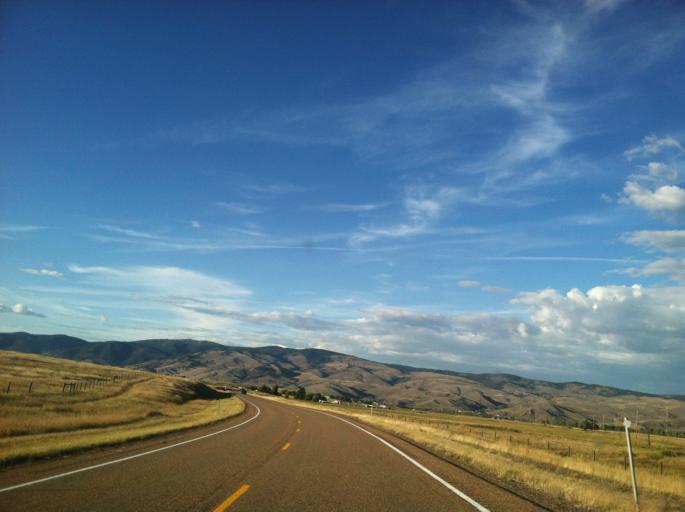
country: US
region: Montana
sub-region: Granite County
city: Philipsburg
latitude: 46.6259
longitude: -113.1702
